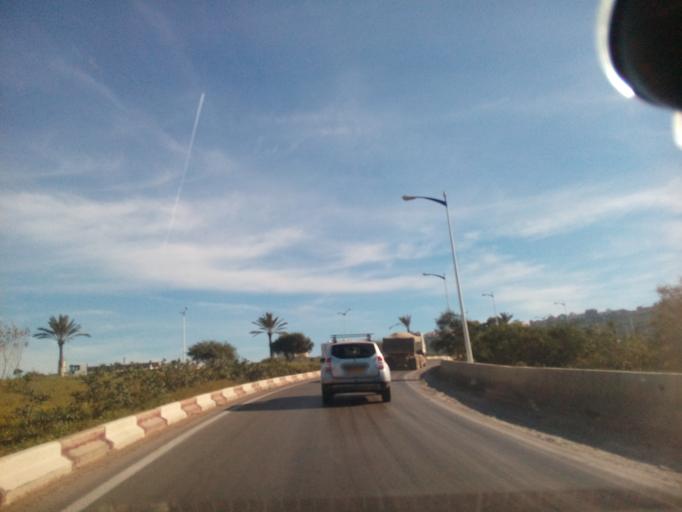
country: DZ
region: Mostaganem
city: Mostaganem
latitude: 35.9110
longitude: 0.0748
